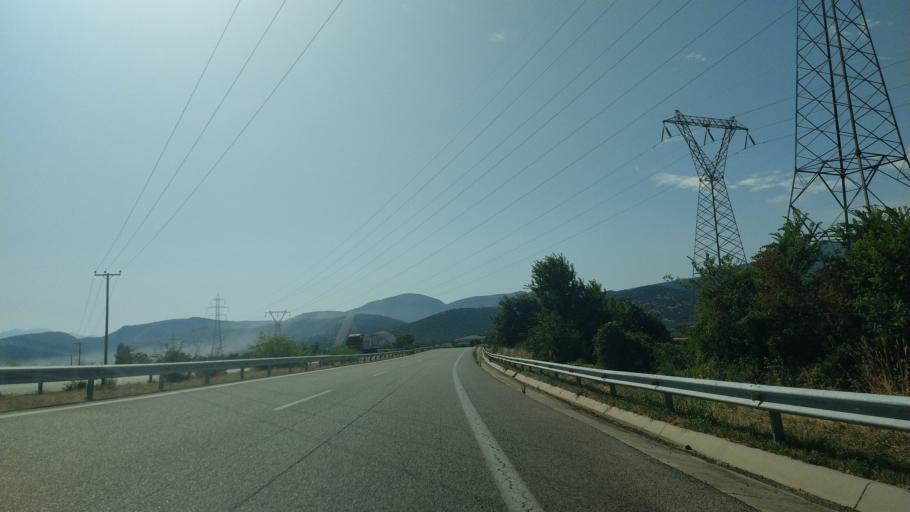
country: GR
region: East Macedonia and Thrace
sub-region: Nomos Kavalas
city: Nea Karvali
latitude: 40.9676
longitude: 24.5189
